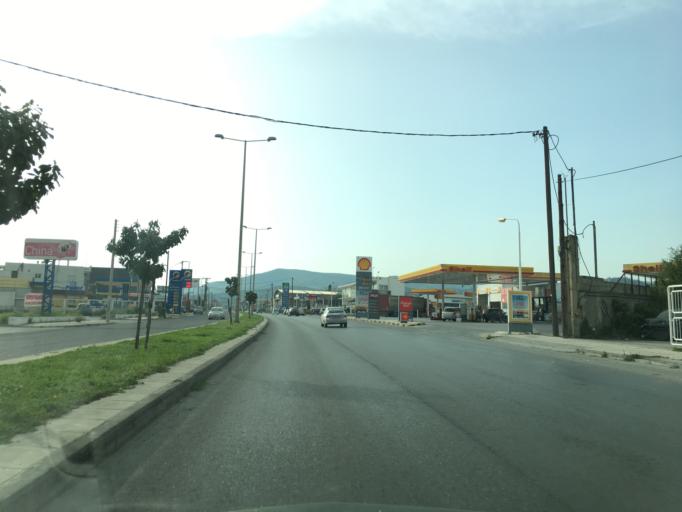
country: GR
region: Thessaly
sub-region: Nomos Magnisias
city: Nea Ionia
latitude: 39.3688
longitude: 22.9194
